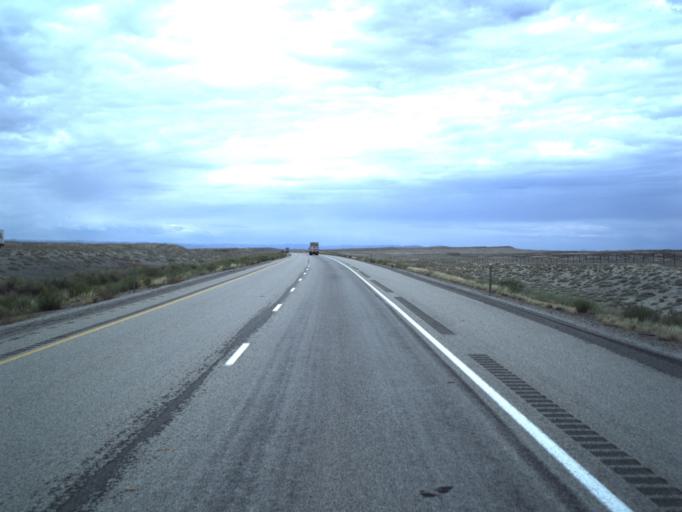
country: US
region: Utah
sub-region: Grand County
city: Moab
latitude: 39.0014
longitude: -109.3182
